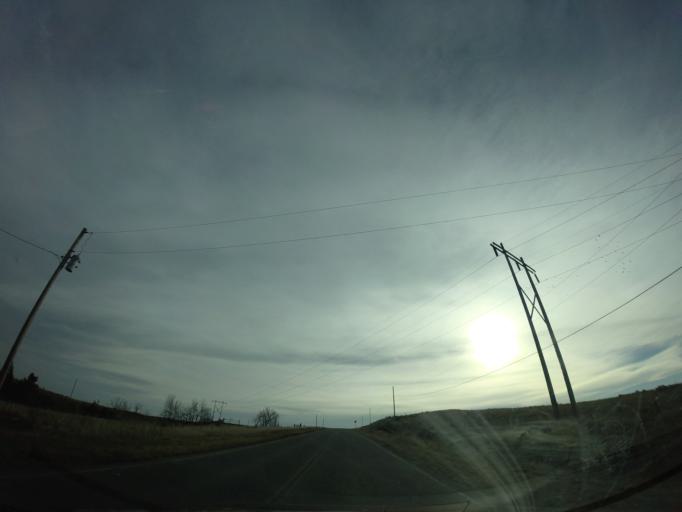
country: US
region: Montana
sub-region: Yellowstone County
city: Billings
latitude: 45.7931
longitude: -108.4555
